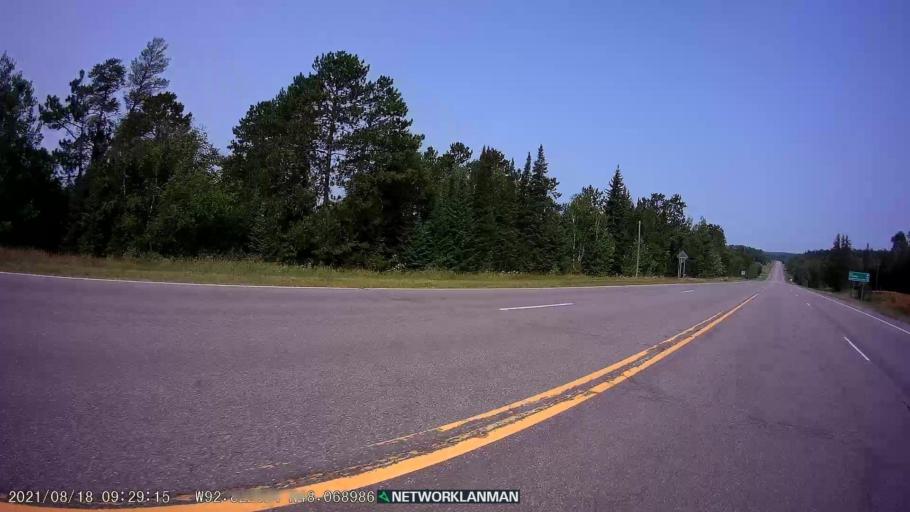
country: US
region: Minnesota
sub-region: Saint Louis County
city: Mountain Iron
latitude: 48.0689
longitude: -92.8225
